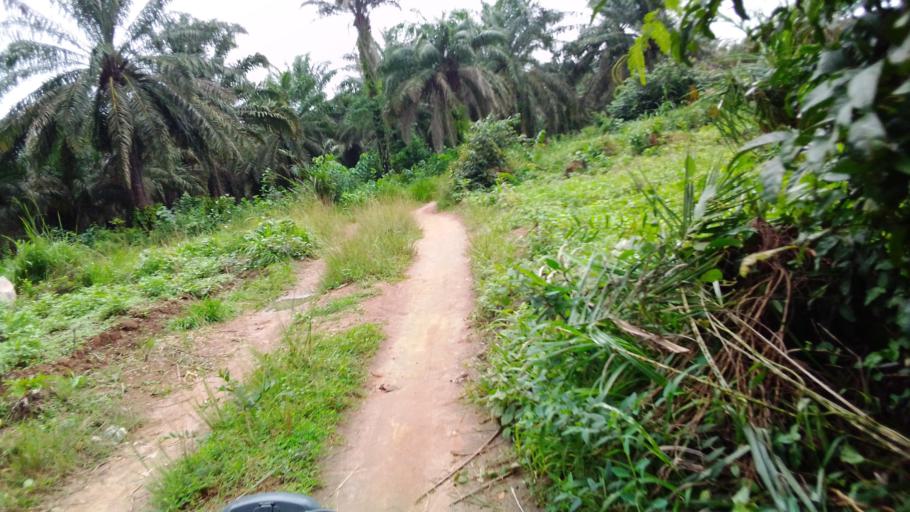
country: SL
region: Eastern Province
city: Kenema
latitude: 7.8679
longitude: -11.1680
